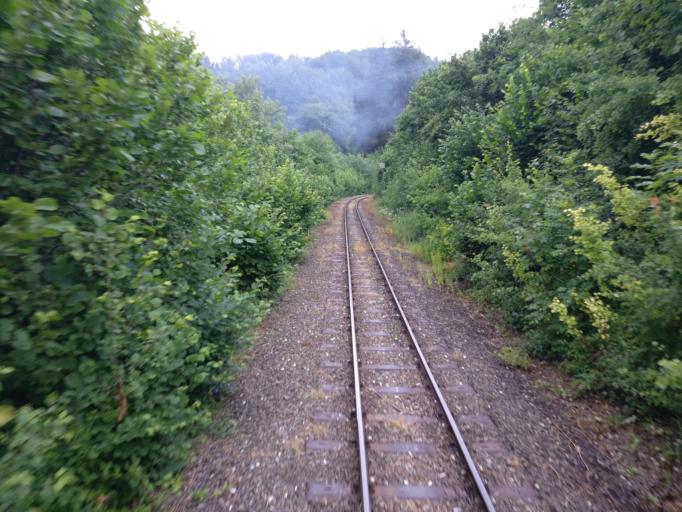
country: AT
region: Upper Austria
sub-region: Politischer Bezirk Steyr-Land
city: Waldneukirchen
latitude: 47.9947
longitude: 14.2793
